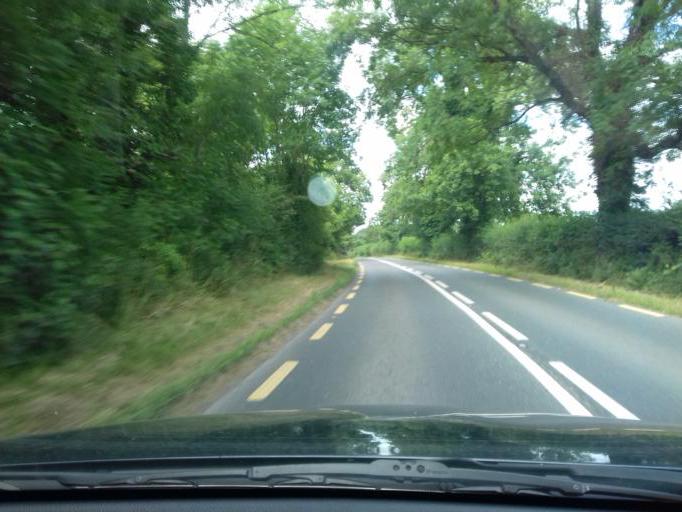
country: IE
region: Leinster
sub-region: Wicklow
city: Baltinglass
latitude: 52.9634
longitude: -6.6960
